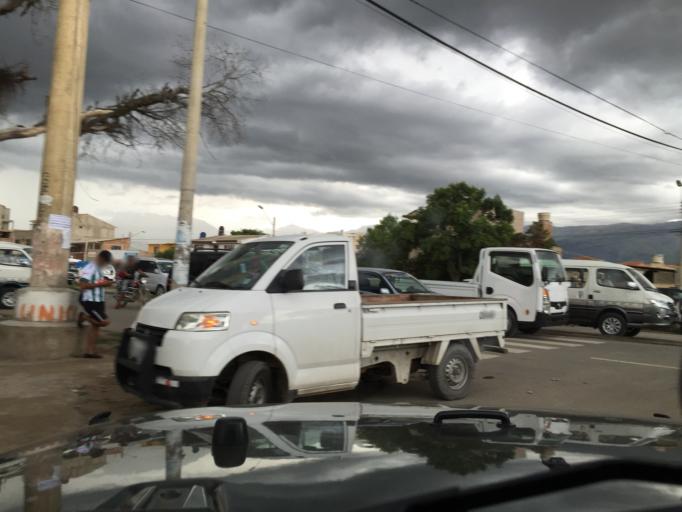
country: BO
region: Cochabamba
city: Cochabamba
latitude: -17.4006
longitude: -66.1878
